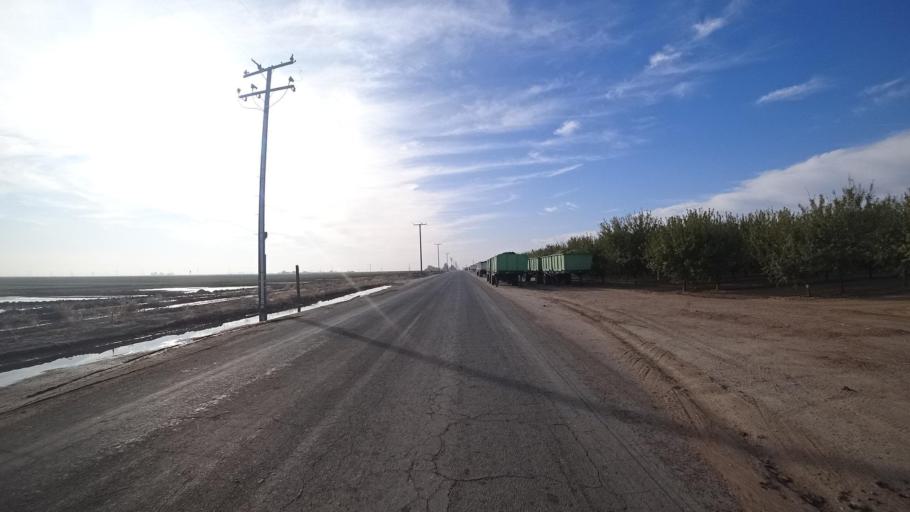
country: US
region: California
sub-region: Kern County
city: Delano
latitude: 35.7822
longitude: -119.2053
